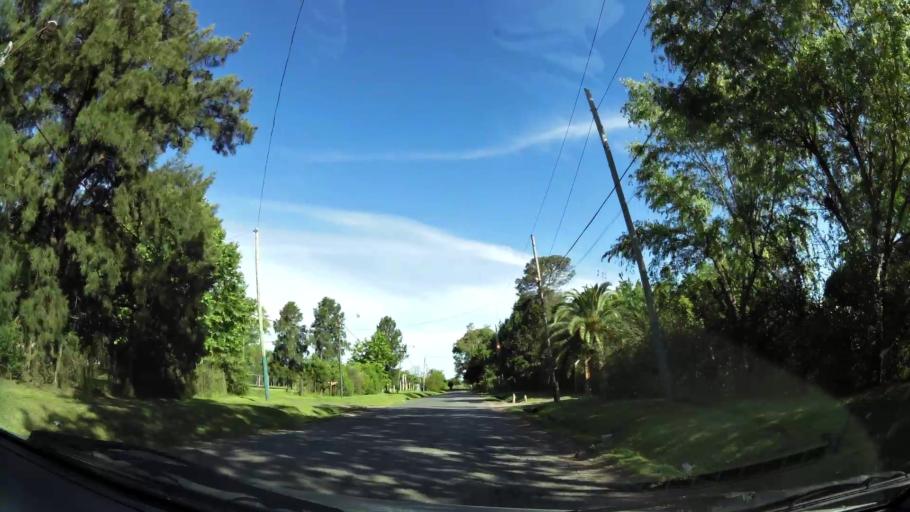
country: AR
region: Buenos Aires
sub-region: Partido de Almirante Brown
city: Adrogue
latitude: -34.8299
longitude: -58.3500
